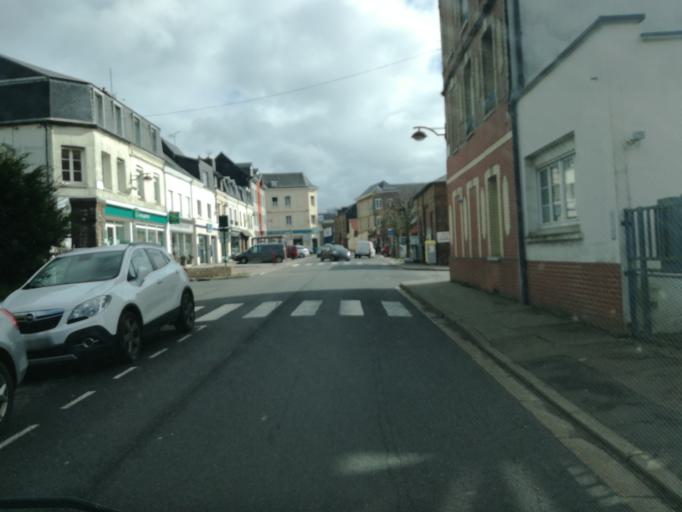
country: FR
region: Haute-Normandie
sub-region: Departement de la Seine-Maritime
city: Fauville-en-Caux
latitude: 49.6523
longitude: 0.5907
